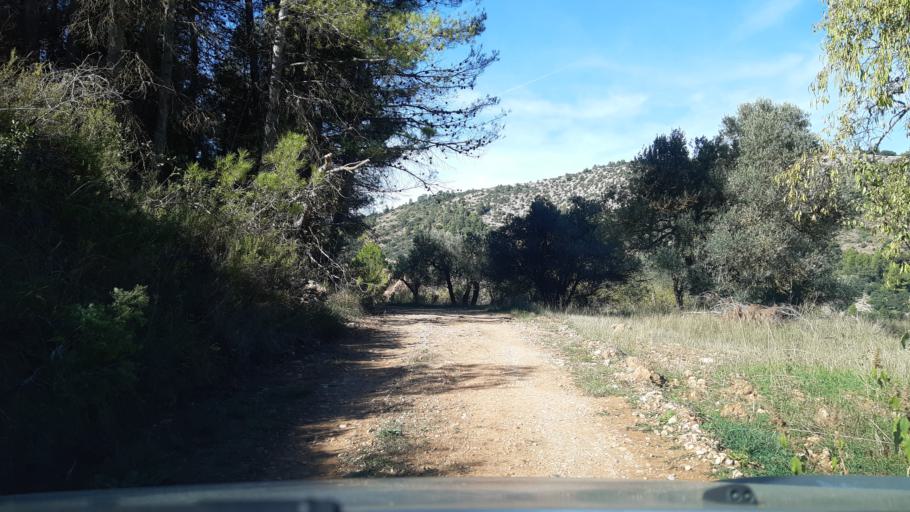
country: ES
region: Aragon
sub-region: Provincia de Teruel
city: Valderrobres
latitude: 40.8406
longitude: 0.2036
